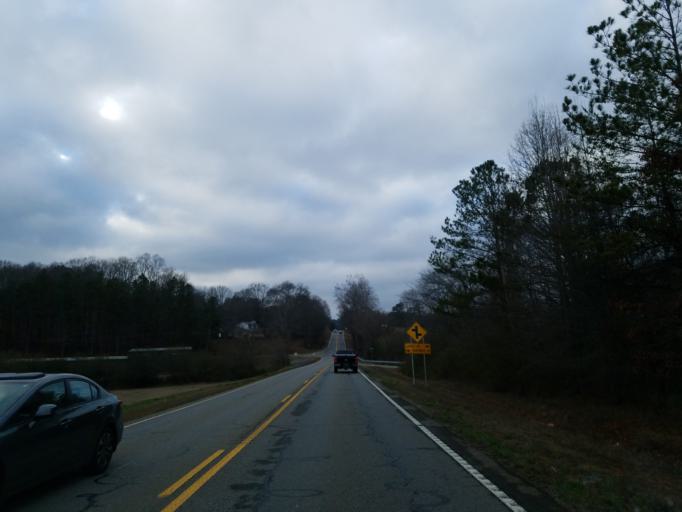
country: US
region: Georgia
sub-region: Cherokee County
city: Canton
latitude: 34.3037
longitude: -84.5249
